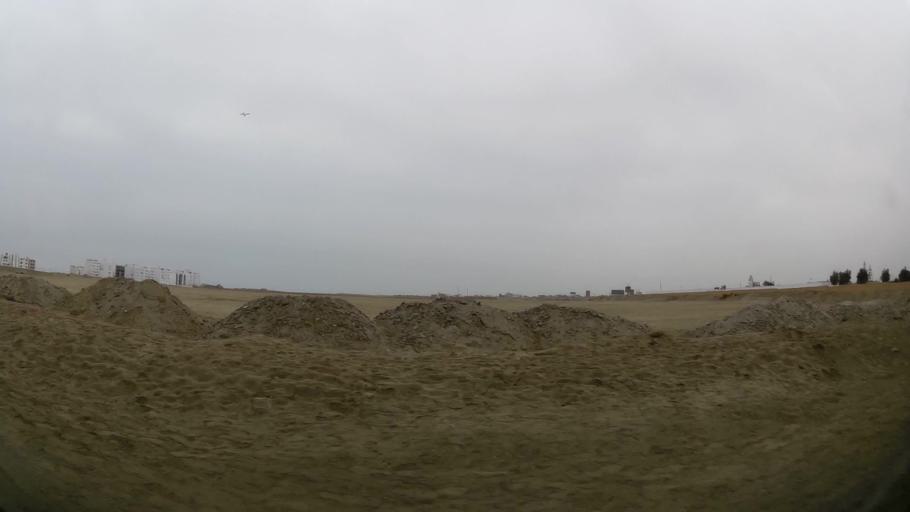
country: PE
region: Lima
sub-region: Lima
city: Punta Hermosa
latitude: -12.3267
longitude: -76.8297
